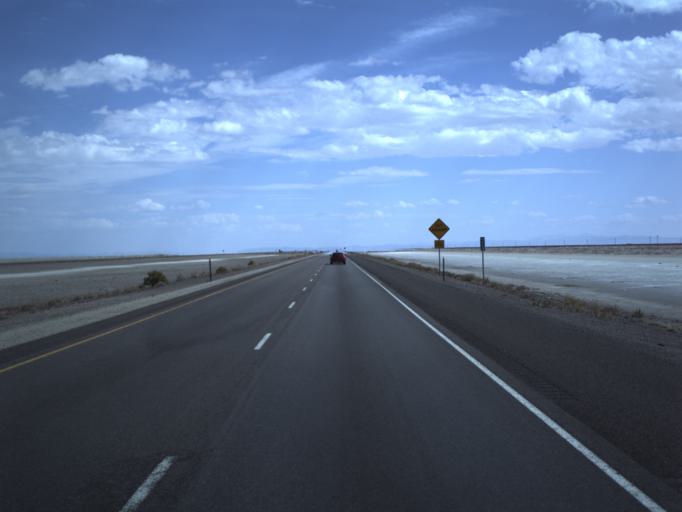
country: US
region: Utah
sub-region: Tooele County
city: Wendover
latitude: 40.7374
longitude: -113.7993
